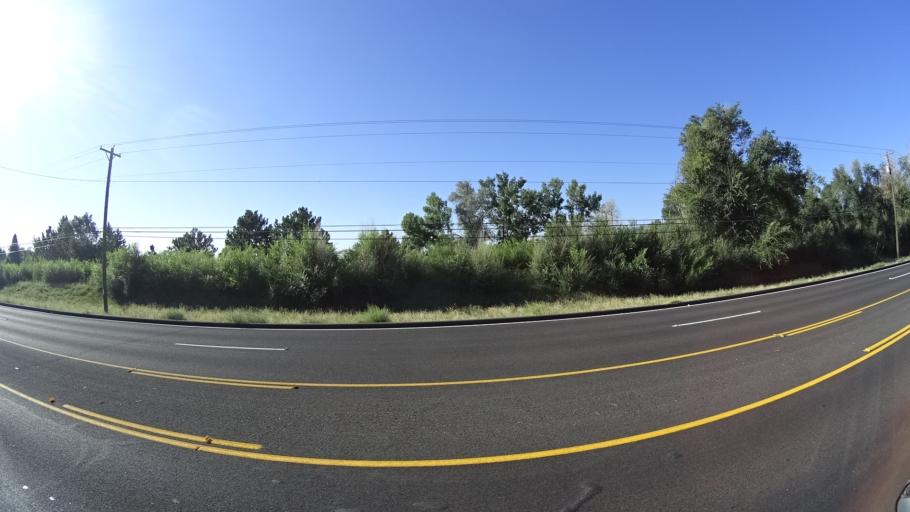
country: US
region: Colorado
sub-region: El Paso County
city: Colorado Springs
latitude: 38.8593
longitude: -104.7815
